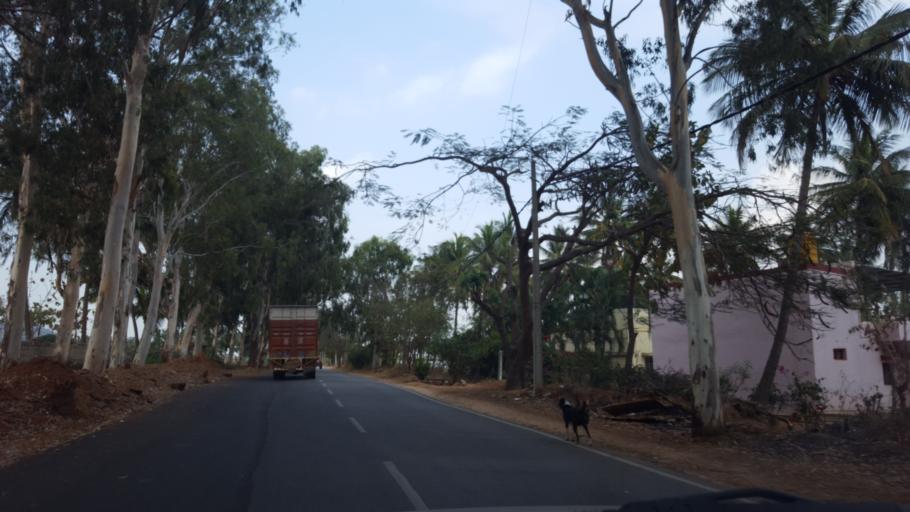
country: IN
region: Karnataka
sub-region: Chikkaballapur
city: Chik Ballapur
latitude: 13.3500
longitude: 77.6873
